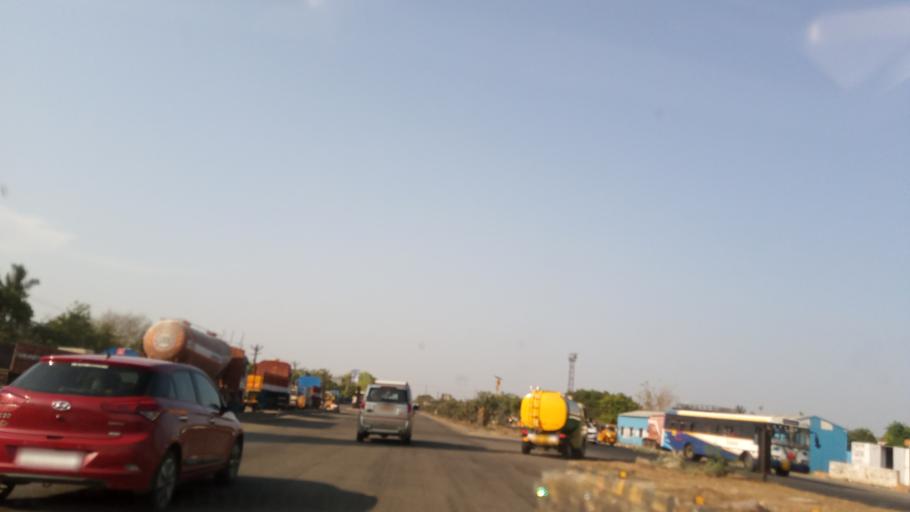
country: IN
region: Tamil Nadu
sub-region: Kancheepuram
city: Poonamalle
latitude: 13.0514
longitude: 80.0894
